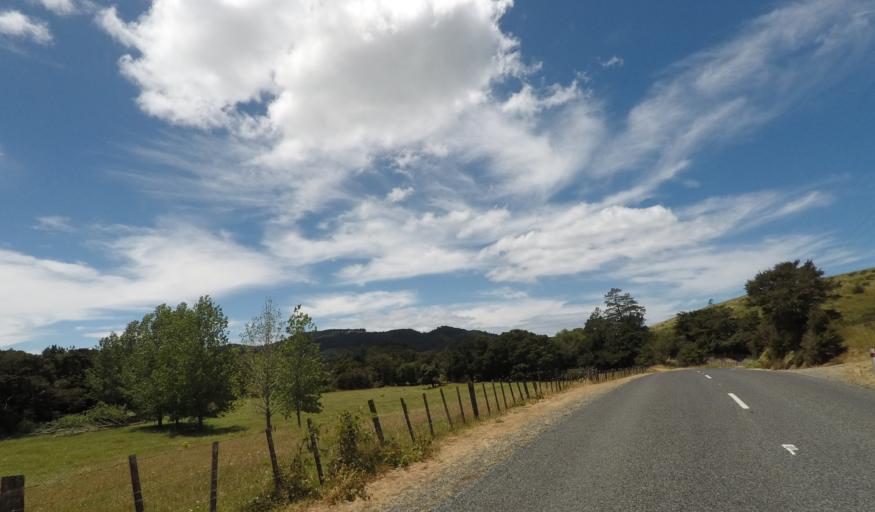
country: NZ
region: Northland
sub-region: Whangarei
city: Ngunguru
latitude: -35.5069
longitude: 174.4222
